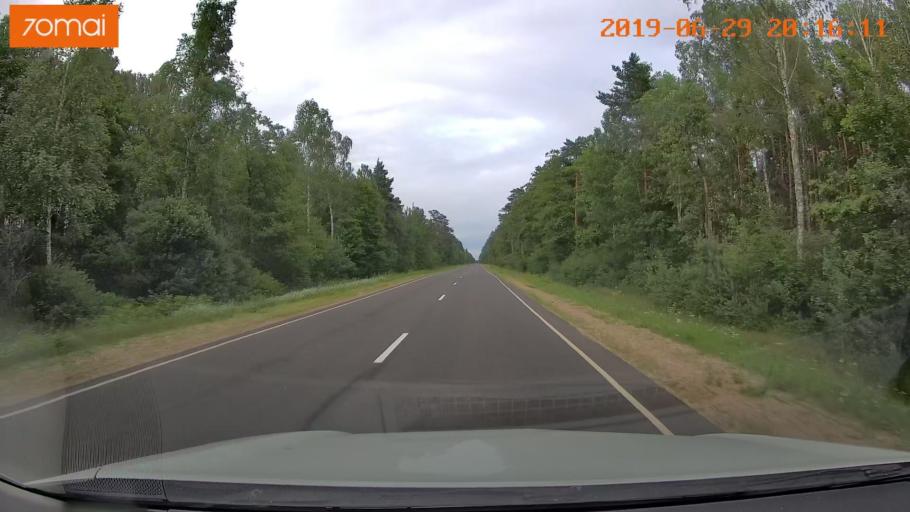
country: BY
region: Brest
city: Asnyezhytsy
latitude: 52.3794
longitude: 26.1909
